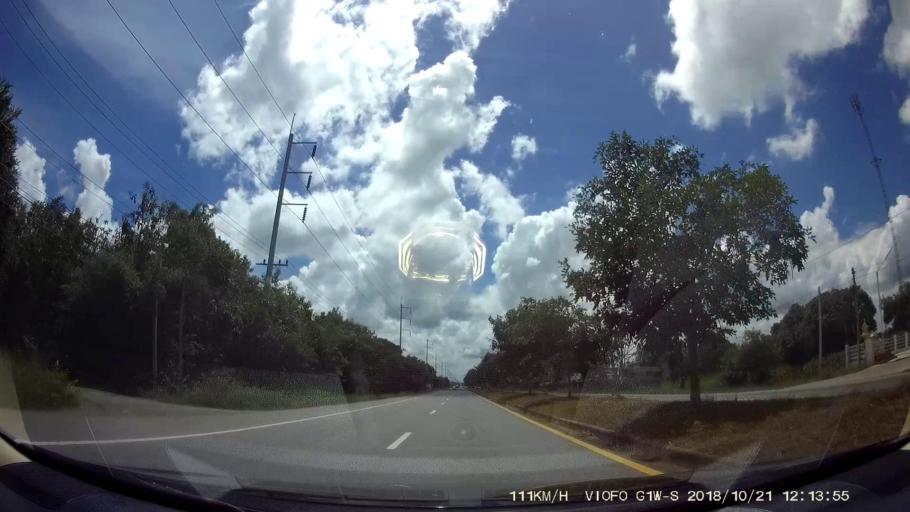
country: TH
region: Chaiyaphum
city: Chatturat
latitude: 15.3854
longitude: 101.8377
